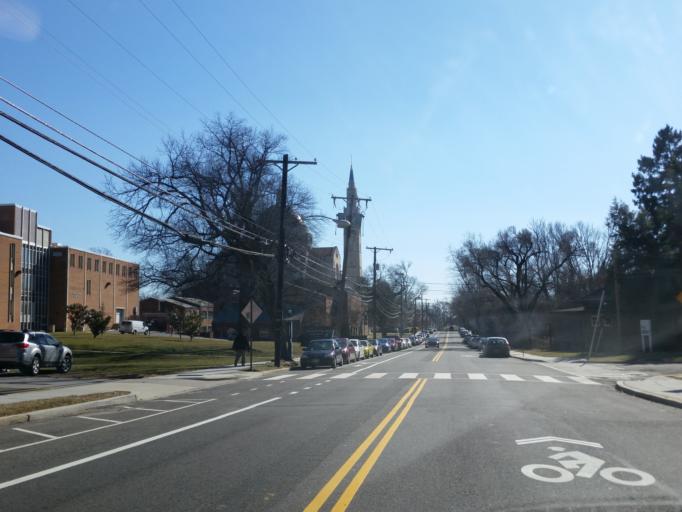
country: US
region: Maryland
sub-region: Prince George's County
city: Chillum
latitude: 38.9365
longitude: -77.0022
